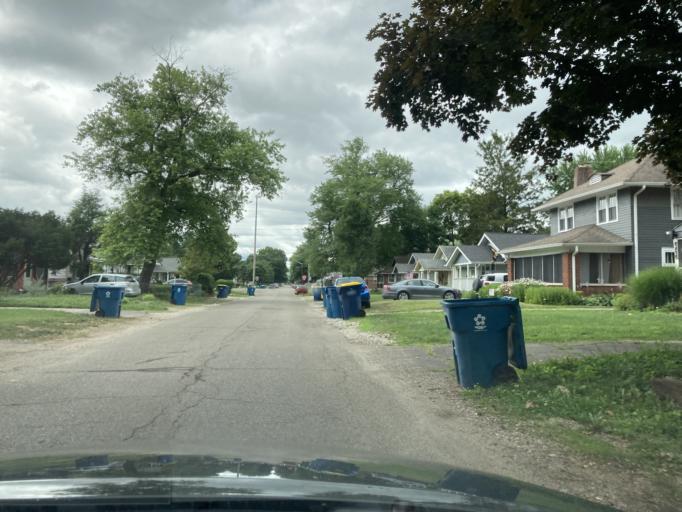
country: US
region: Indiana
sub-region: Marion County
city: Broad Ripple
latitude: 39.8440
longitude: -86.1314
